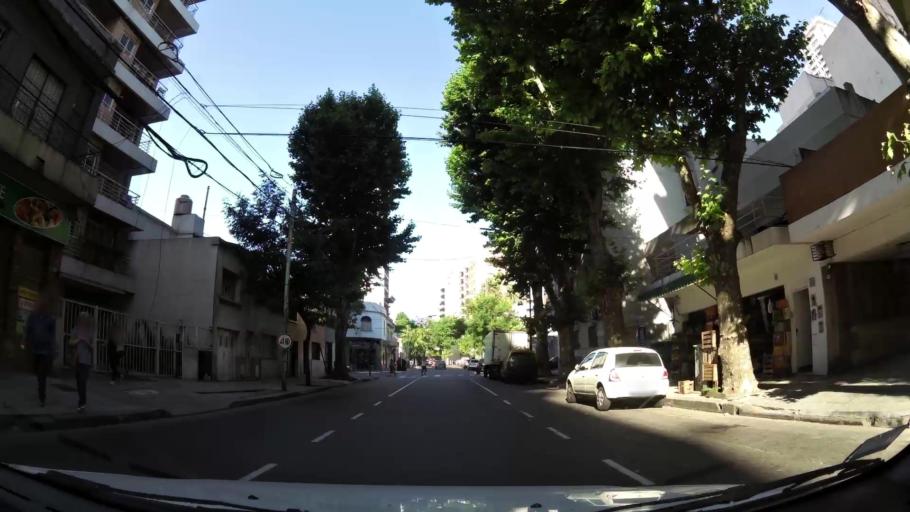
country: AR
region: Buenos Aires F.D.
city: Villa Santa Rita
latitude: -34.6177
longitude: -58.4471
